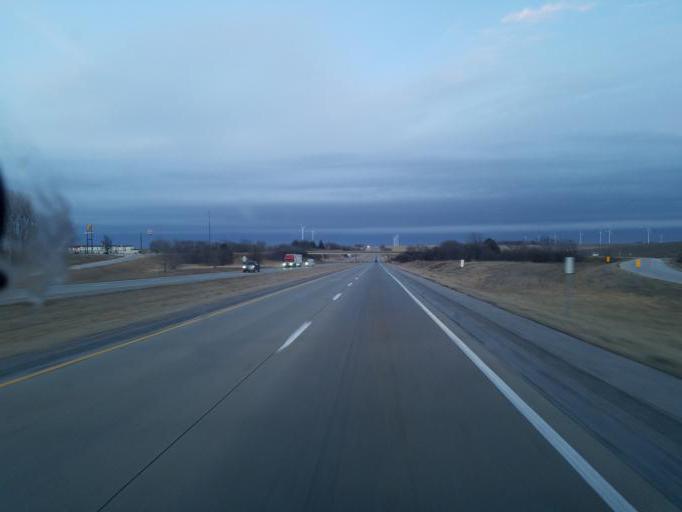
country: US
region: Iowa
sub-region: Pottawattamie County
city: Avoca
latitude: 41.4972
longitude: -95.2262
